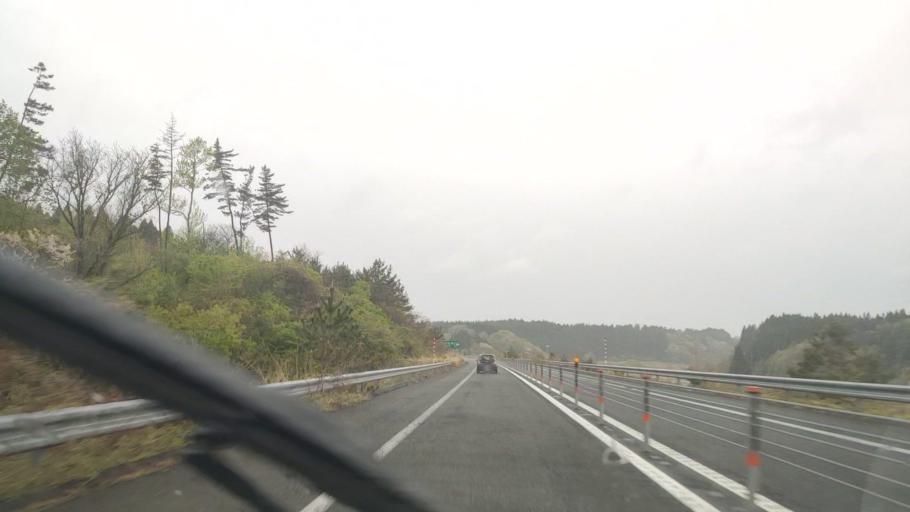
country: JP
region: Akita
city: Noshiromachi
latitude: 40.1925
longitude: 140.1122
